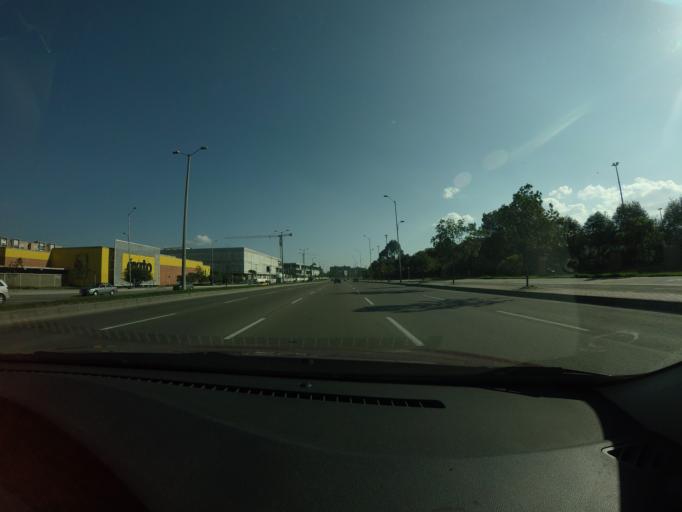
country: CO
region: Cundinamarca
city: Cota
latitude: 4.7354
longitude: -74.0667
